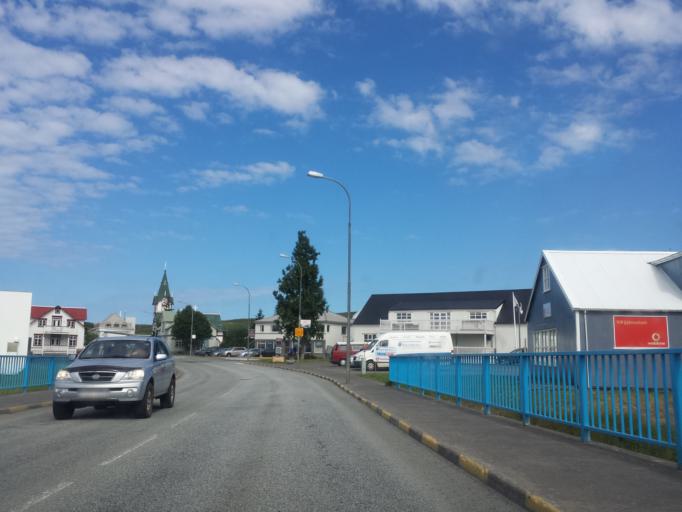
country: IS
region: Northeast
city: Husavik
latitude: 66.0443
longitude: -17.3417
